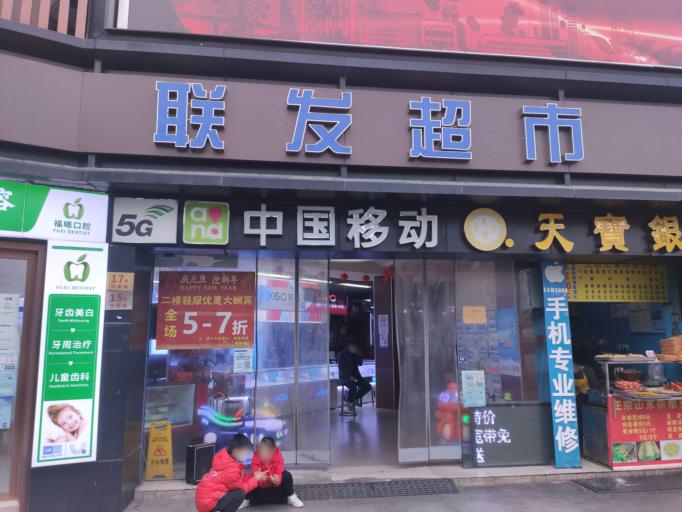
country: CN
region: Shanghai Shi
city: Huacao
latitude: 31.2077
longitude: 121.2928
